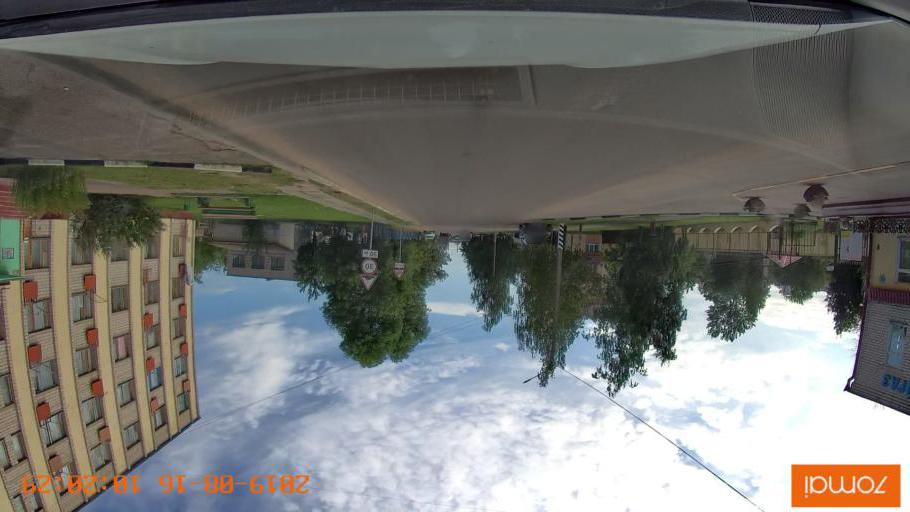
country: BY
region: Mogilev
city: Asipovichy
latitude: 53.2998
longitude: 28.6613
